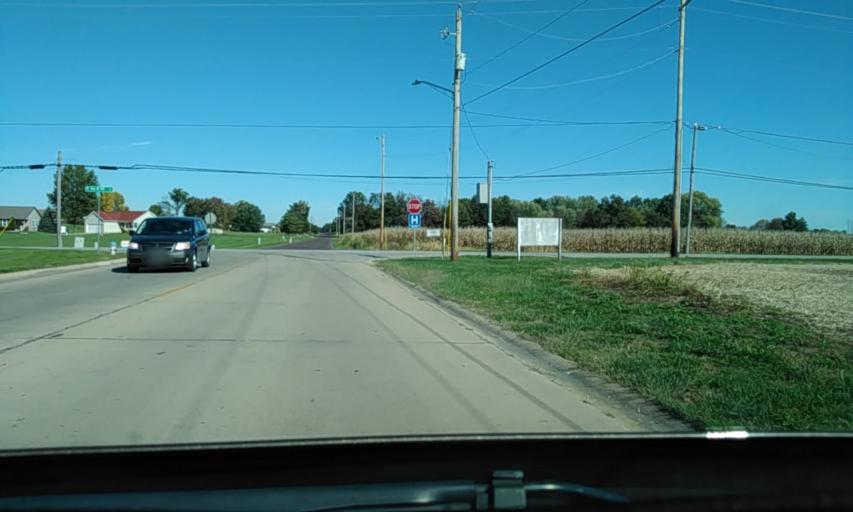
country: US
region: Illinois
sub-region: Bond County
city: Greenville
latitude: 38.9015
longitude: -89.3913
